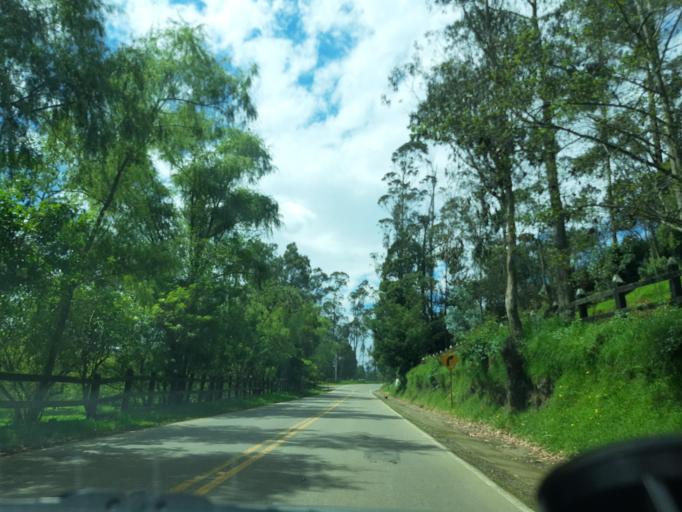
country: CO
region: Boyaca
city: Chiquinquira
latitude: 5.6089
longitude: -73.7358
